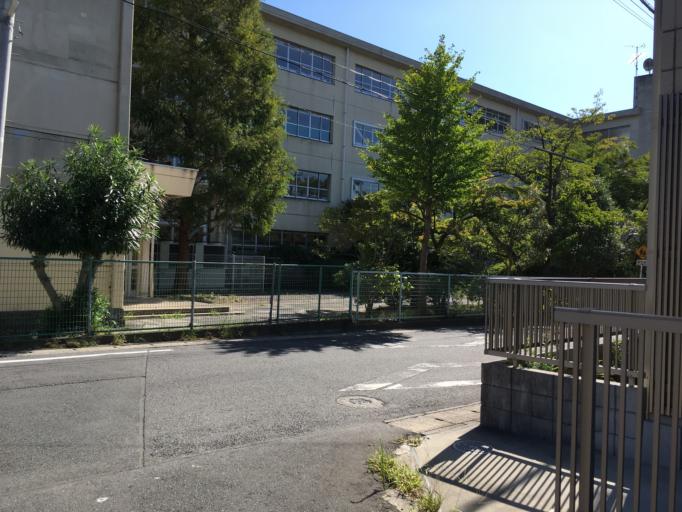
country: JP
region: Chiba
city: Matsudo
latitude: 35.8100
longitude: 139.9254
